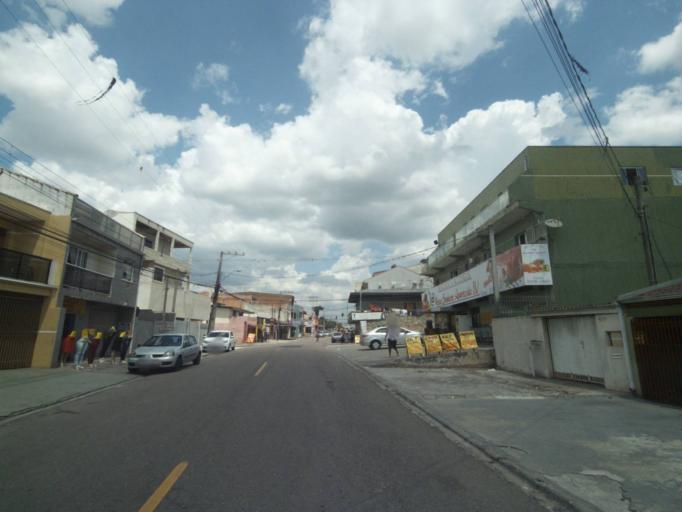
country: BR
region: Parana
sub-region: Sao Jose Dos Pinhais
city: Sao Jose dos Pinhais
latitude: -25.5325
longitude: -49.2750
